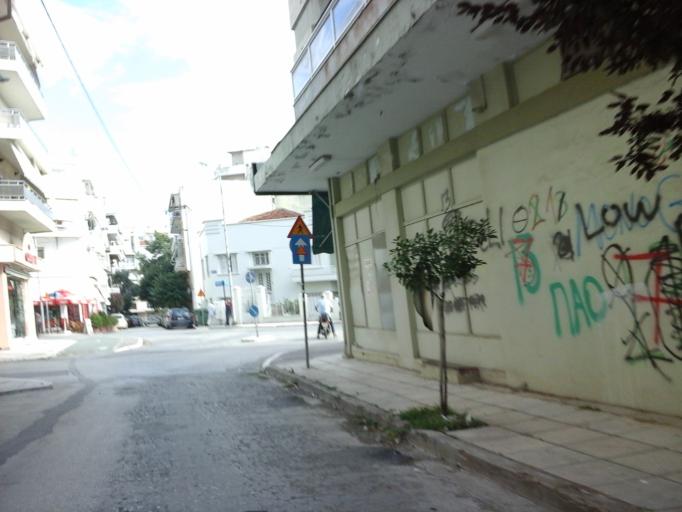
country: GR
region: East Macedonia and Thrace
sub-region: Nomos Evrou
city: Alexandroupoli
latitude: 40.8445
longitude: 25.8691
